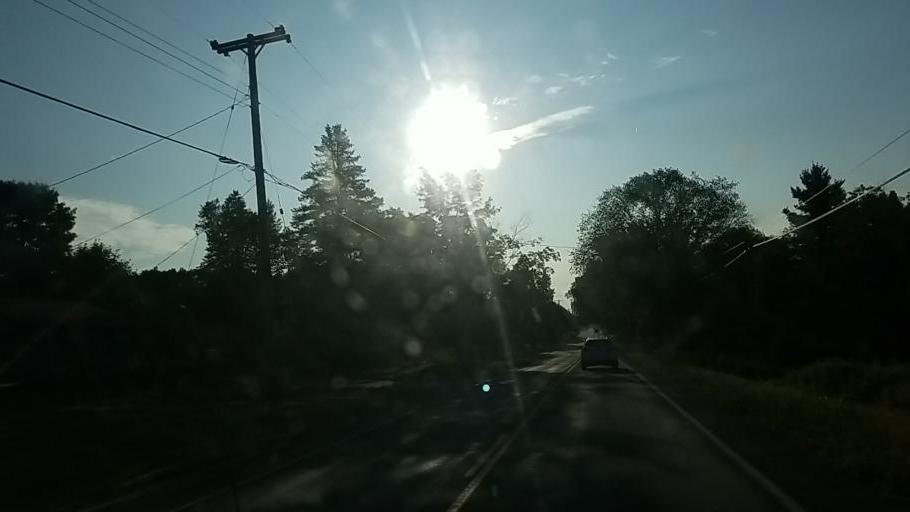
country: US
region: Michigan
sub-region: Montcalm County
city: Stanton
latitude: 43.2500
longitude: -85.1279
